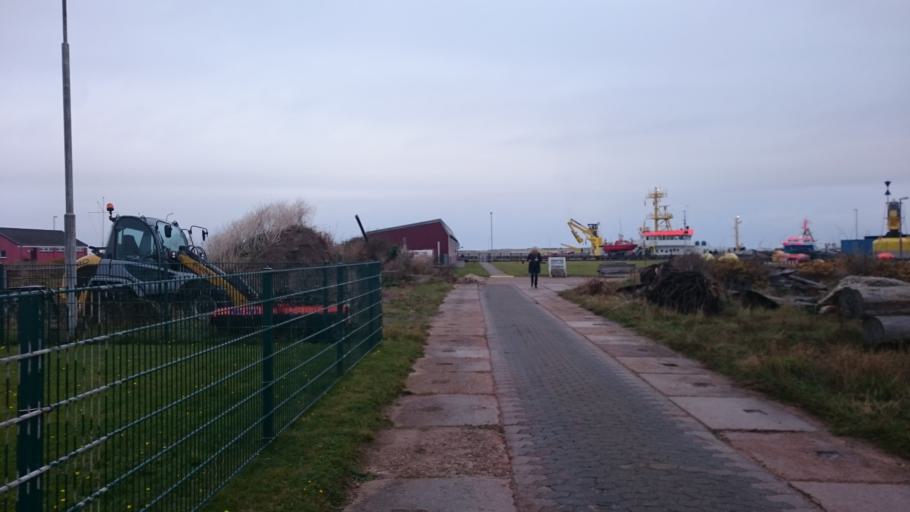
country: DE
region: Schleswig-Holstein
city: Helgoland
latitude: 54.1749
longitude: 7.8921
